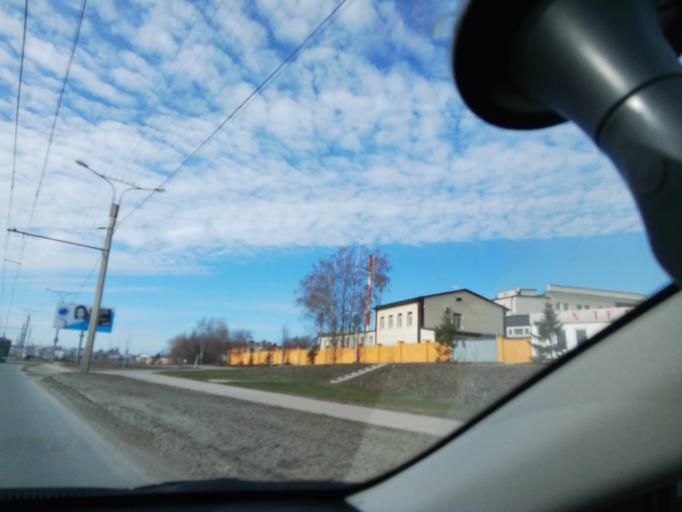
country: RU
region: Chuvashia
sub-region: Cheboksarskiy Rayon
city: Cheboksary
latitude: 56.1201
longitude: 47.2503
